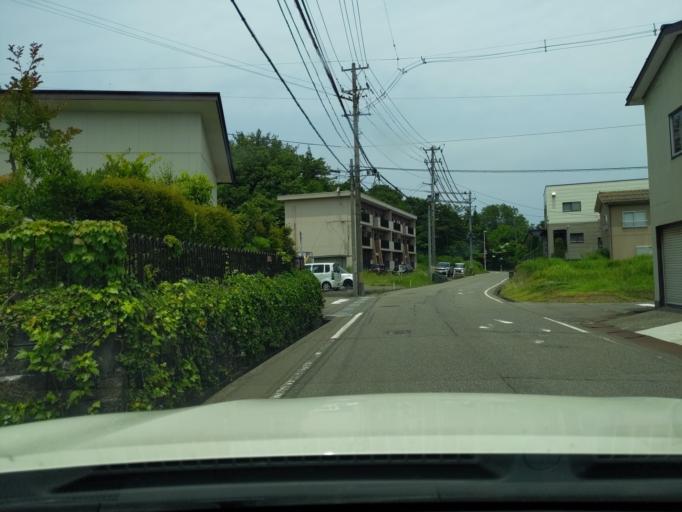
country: JP
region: Niigata
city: Kashiwazaki
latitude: 37.3554
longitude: 138.5408
